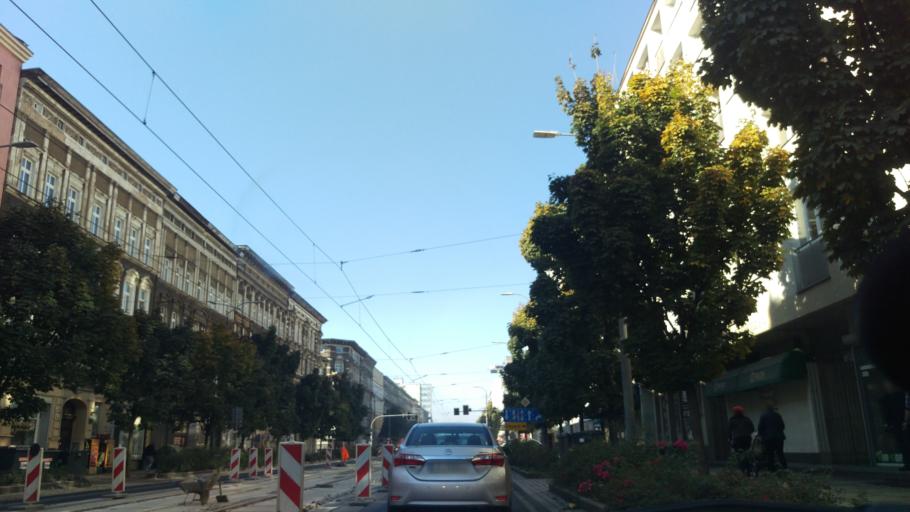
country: PL
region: West Pomeranian Voivodeship
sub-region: Szczecin
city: Szczecin
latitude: 53.4262
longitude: 14.5444
